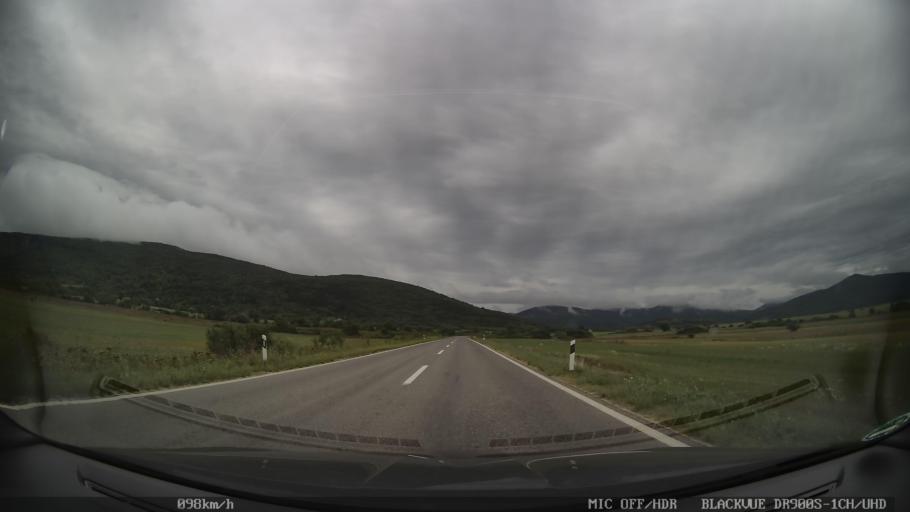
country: HR
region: Licko-Senjska
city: Otocac
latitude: 44.8574
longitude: 15.2891
